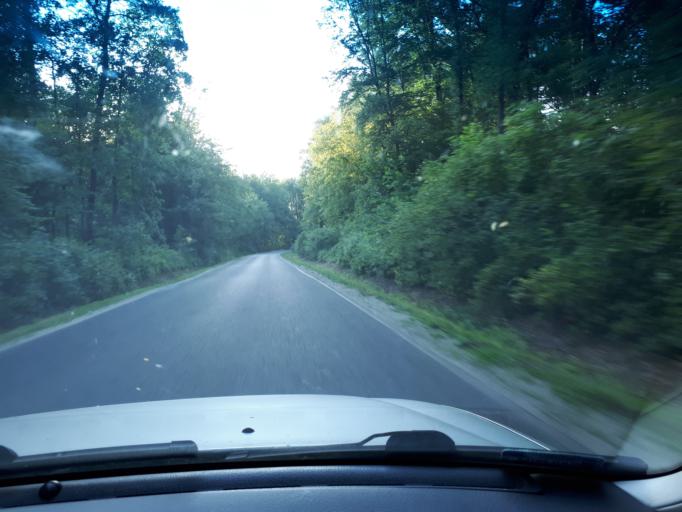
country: PL
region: Subcarpathian Voivodeship
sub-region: Powiat debicki
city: Debica
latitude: 49.9776
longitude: 21.4103
